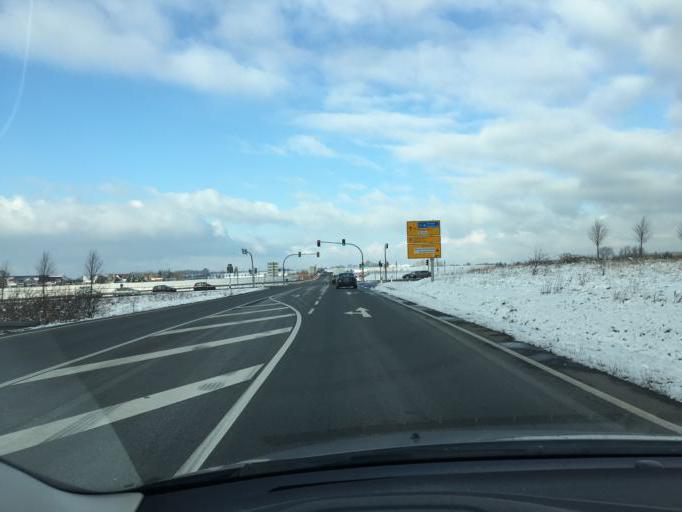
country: DE
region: Saxony
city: Grimma
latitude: 51.2309
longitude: 12.6973
